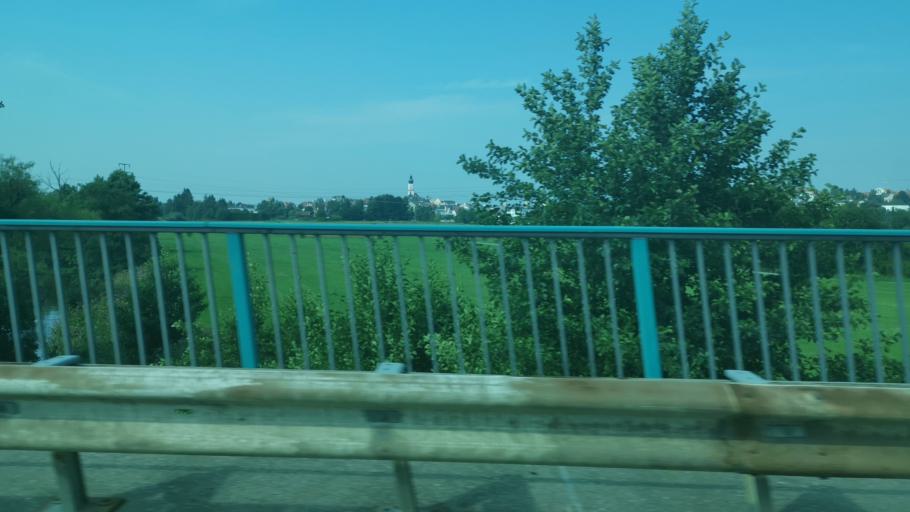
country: DE
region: Bavaria
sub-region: Upper Palatinate
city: Cham
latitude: 49.2192
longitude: 12.6793
